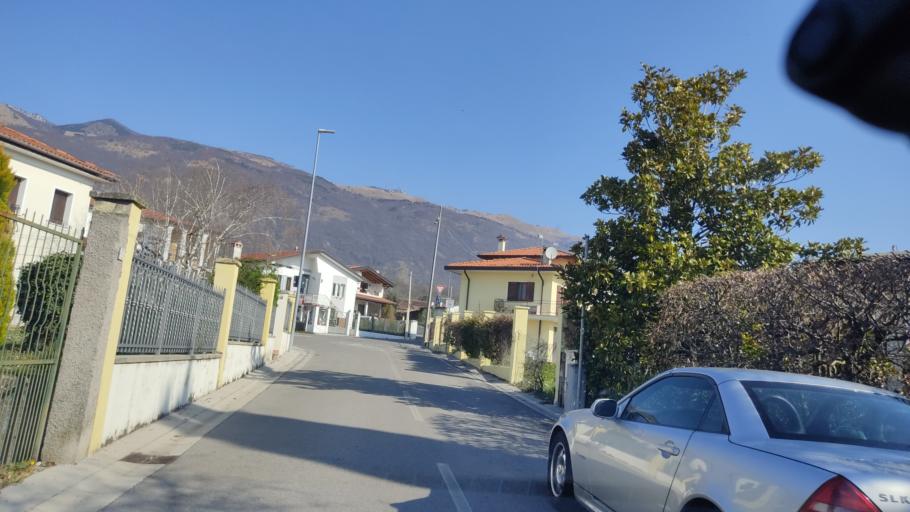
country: IT
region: Friuli Venezia Giulia
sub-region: Provincia di Pordenone
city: Budoia
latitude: 46.0539
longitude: 12.5368
